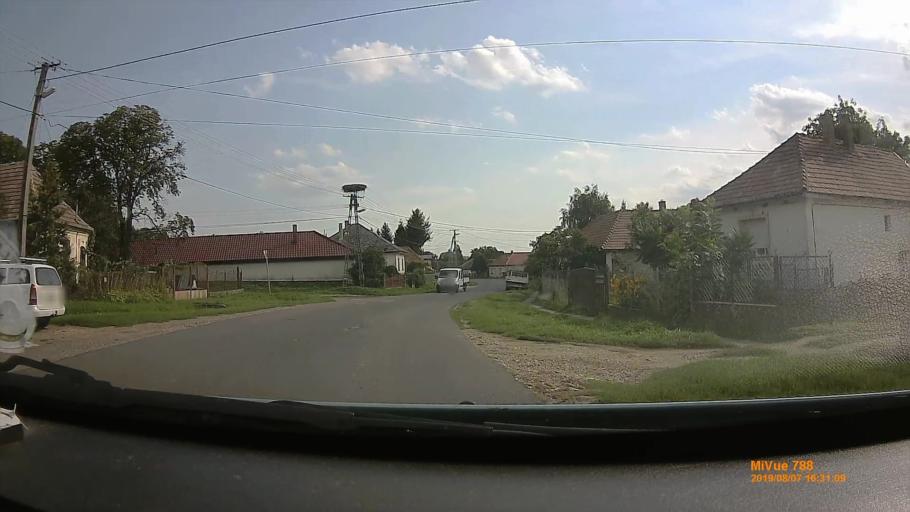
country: HU
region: Borsod-Abauj-Zemplen
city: Gonc
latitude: 48.4511
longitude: 21.2420
